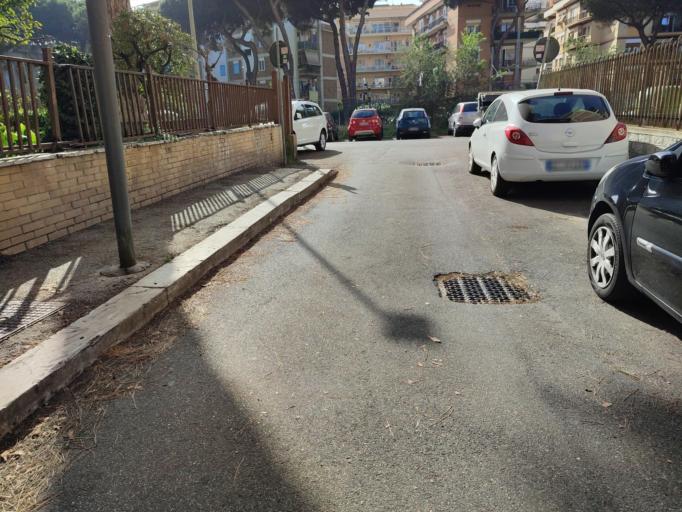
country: IT
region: Latium
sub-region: Citta metropolitana di Roma Capitale
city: Lido di Ostia
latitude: 41.7303
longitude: 12.2919
